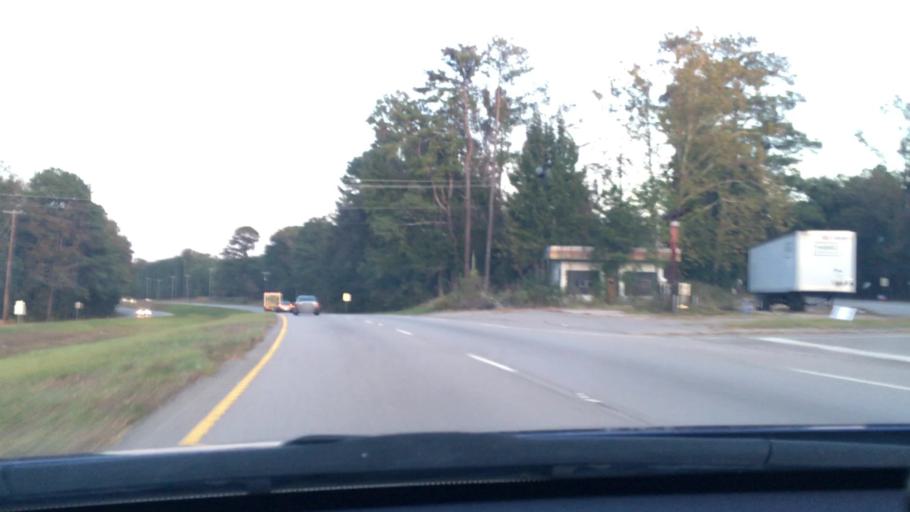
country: US
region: South Carolina
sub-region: Richland County
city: Gadsden
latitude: 33.9426
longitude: -80.7719
